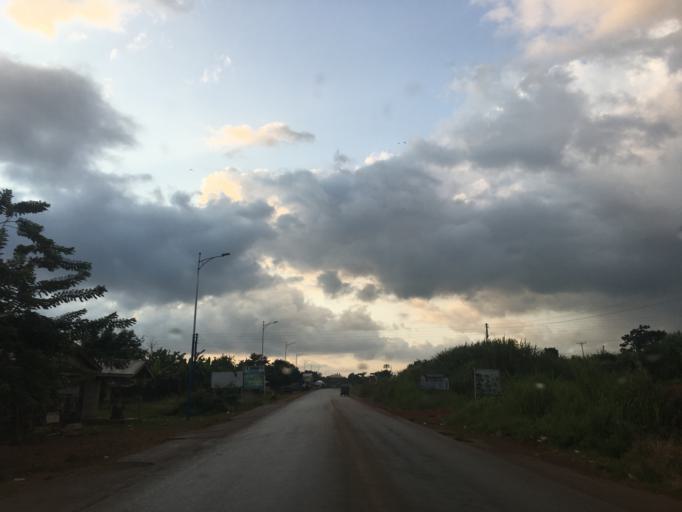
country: GH
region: Western
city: Bibiani
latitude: 6.7802
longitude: -2.5149
